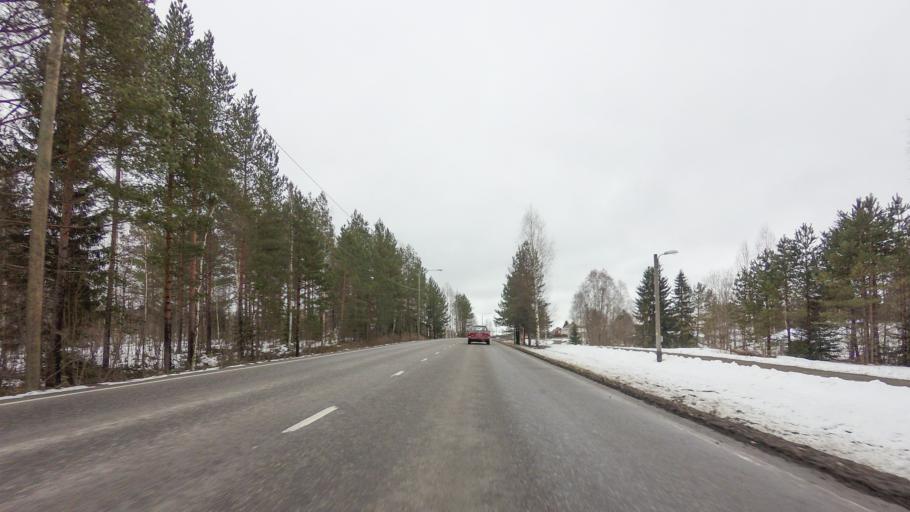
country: FI
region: Southern Savonia
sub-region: Savonlinna
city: Savonlinna
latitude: 61.8800
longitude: 28.9460
